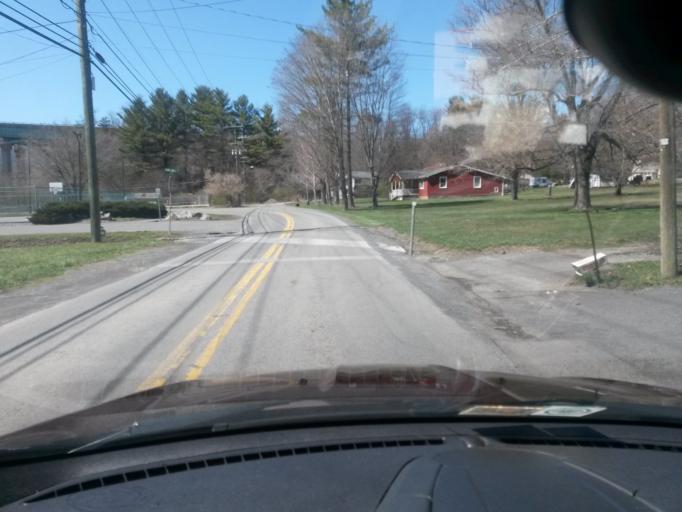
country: US
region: West Virginia
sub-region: Greenbrier County
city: White Sulphur Springs
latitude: 37.7909
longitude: -80.2908
